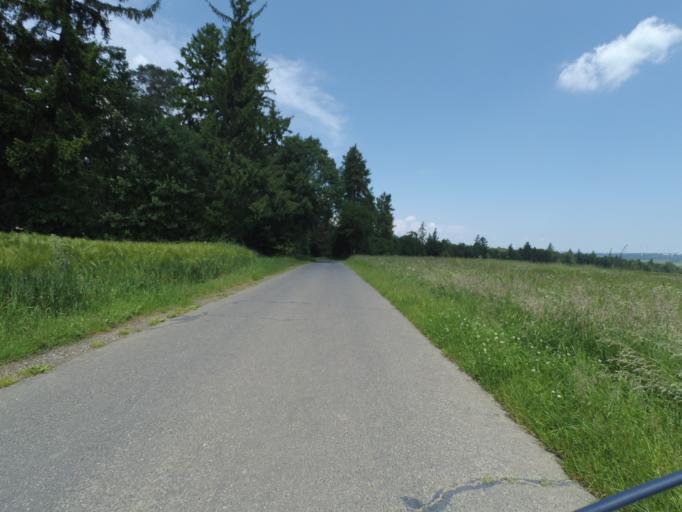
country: DE
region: Rheinland-Pfalz
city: Mermuth
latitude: 50.1673
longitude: 7.4952
